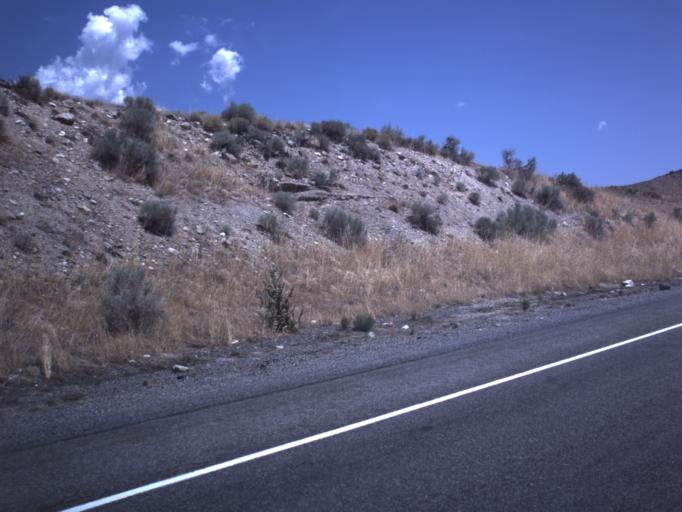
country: US
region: Utah
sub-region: Juab County
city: Nephi
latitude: 39.6316
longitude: -112.1149
